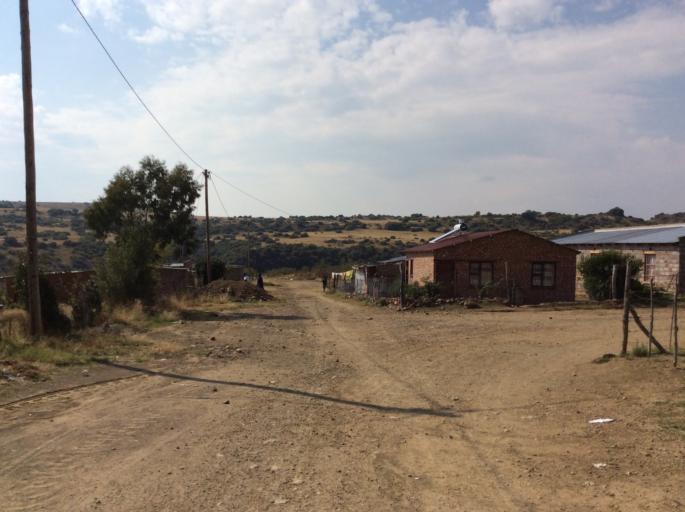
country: LS
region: Mafeteng
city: Mafeteng
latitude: -29.9807
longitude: 27.0087
